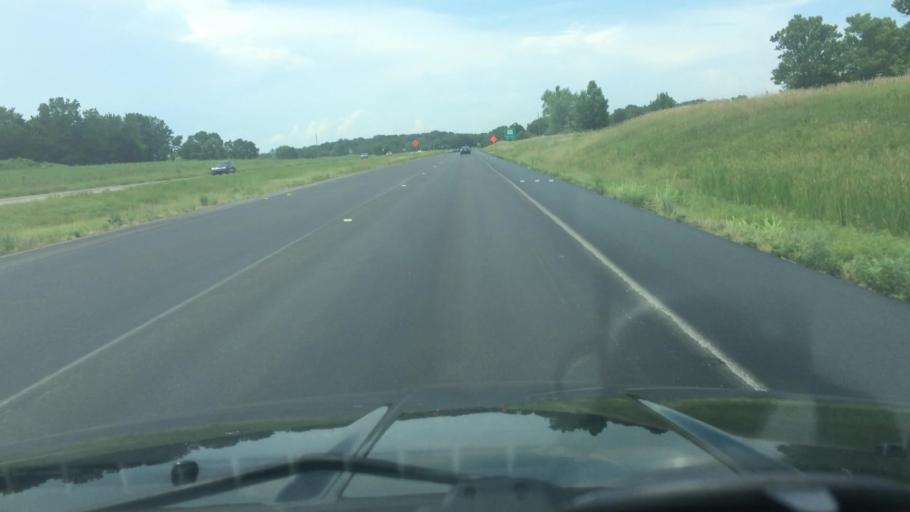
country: US
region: Missouri
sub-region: Saint Clair County
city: Osceola
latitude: 38.0053
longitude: -93.6562
